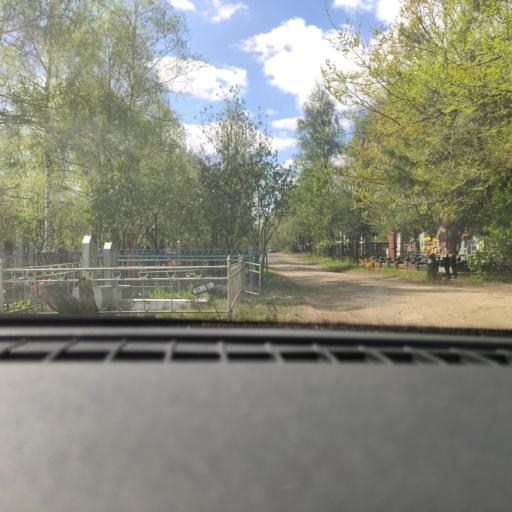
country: RU
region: Voronezj
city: Somovo
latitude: 51.6617
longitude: 39.2989
